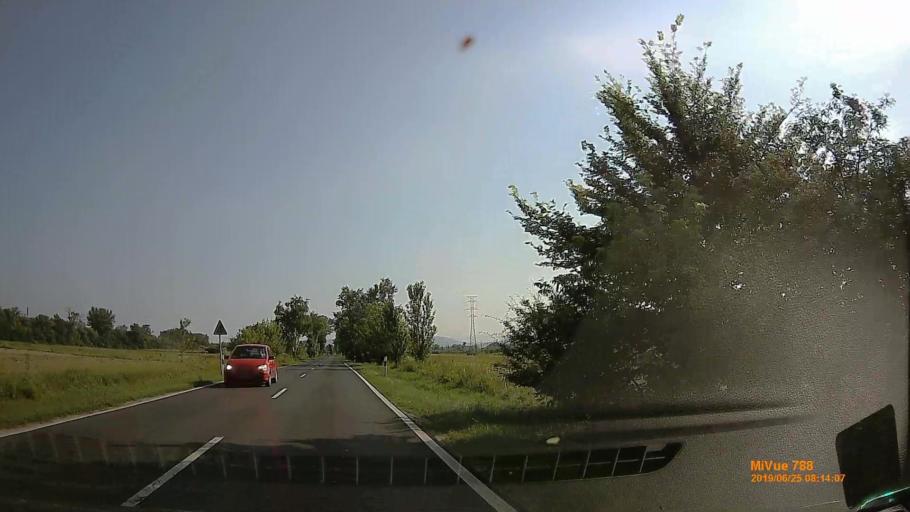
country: HU
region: Komarom-Esztergom
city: Tokod
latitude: 47.7537
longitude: 18.6945
